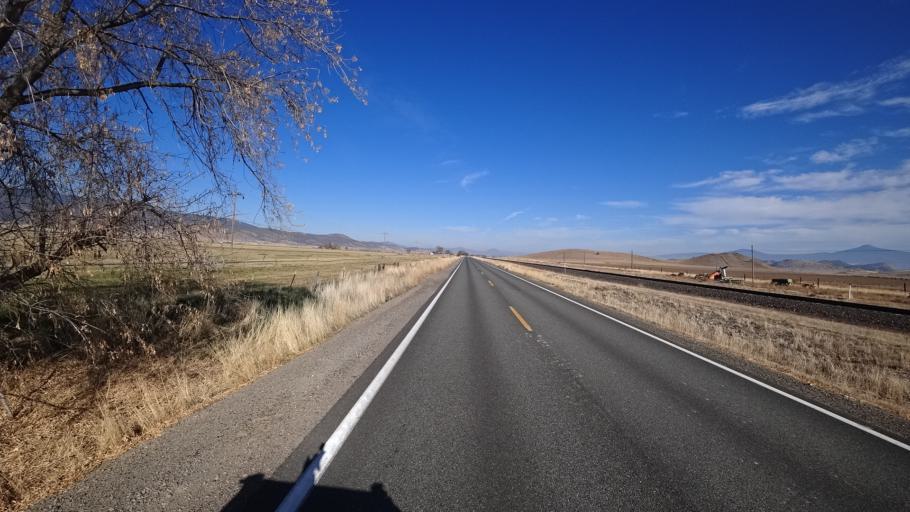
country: US
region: California
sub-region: Siskiyou County
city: Montague
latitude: 41.5460
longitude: -122.5259
